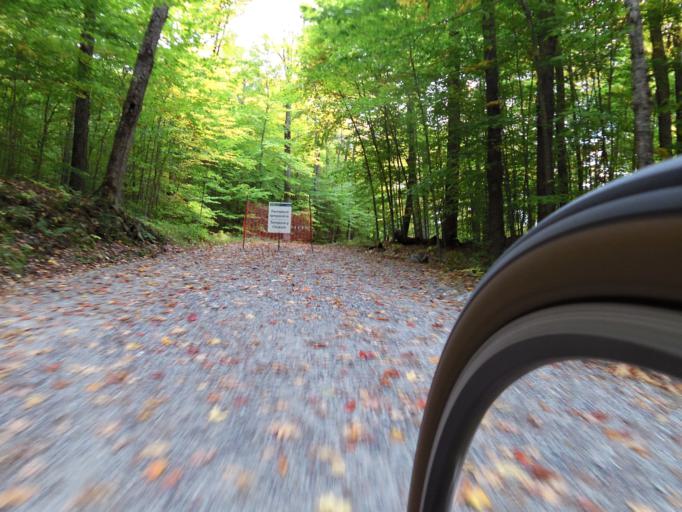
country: CA
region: Quebec
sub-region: Outaouais
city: Wakefield
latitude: 45.6014
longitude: -76.0439
